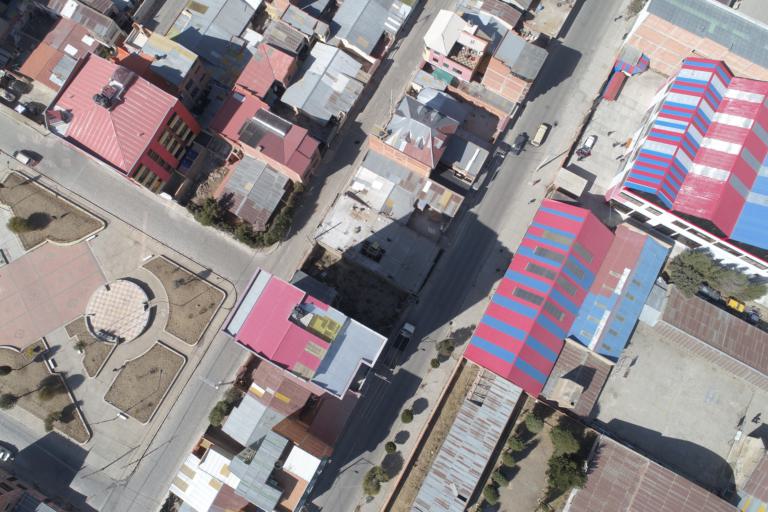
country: BO
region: La Paz
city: La Paz
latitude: -16.5279
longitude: -68.1514
